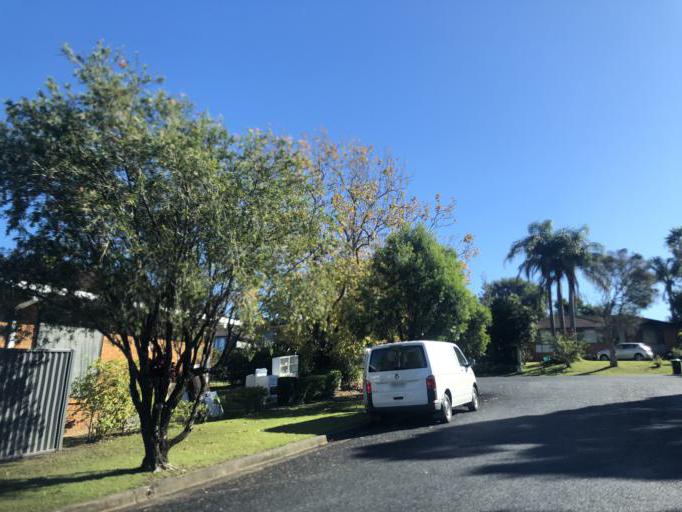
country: AU
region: New South Wales
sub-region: Coffs Harbour
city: Toormina
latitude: -30.3697
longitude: 153.0849
